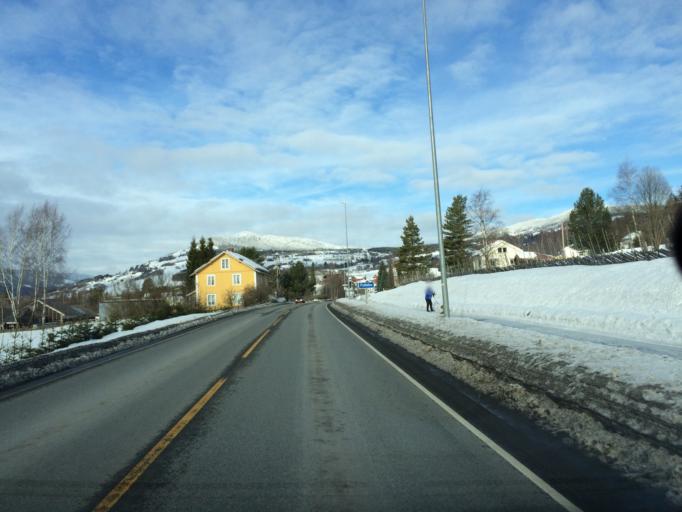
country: NO
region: Oppland
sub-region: Gausdal
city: Segalstad bru
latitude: 61.2102
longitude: 10.2964
